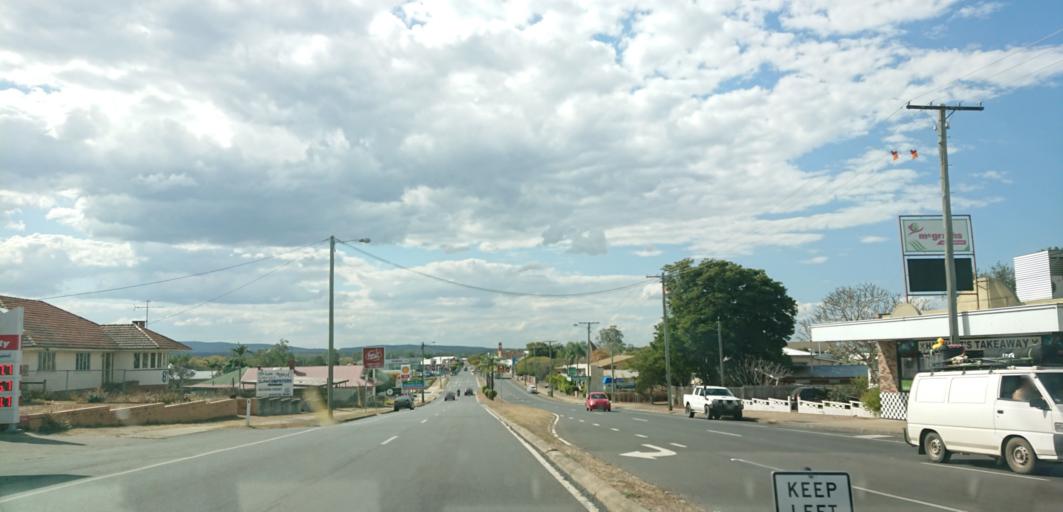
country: AU
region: Queensland
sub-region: Lockyer Valley
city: Gatton
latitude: -27.5612
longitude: 152.2753
